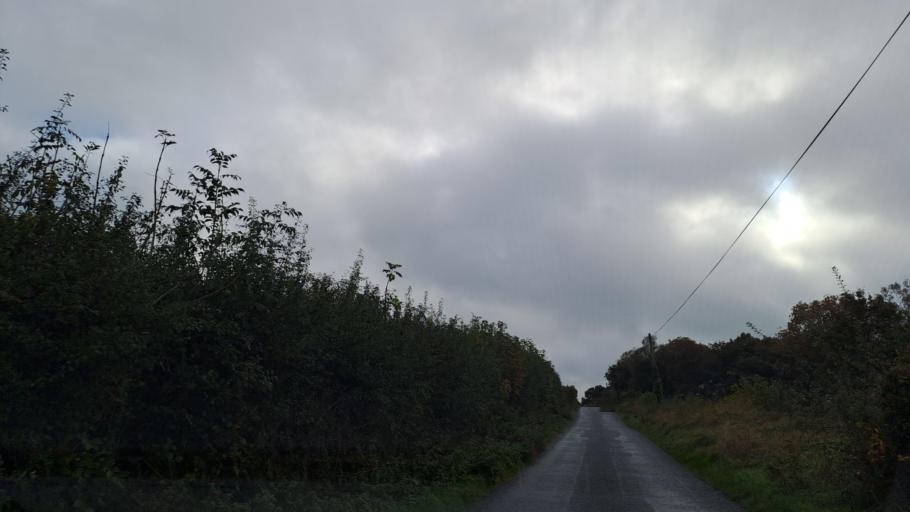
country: IE
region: Ulster
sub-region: An Cabhan
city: Bailieborough
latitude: 53.9769
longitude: -6.9958
